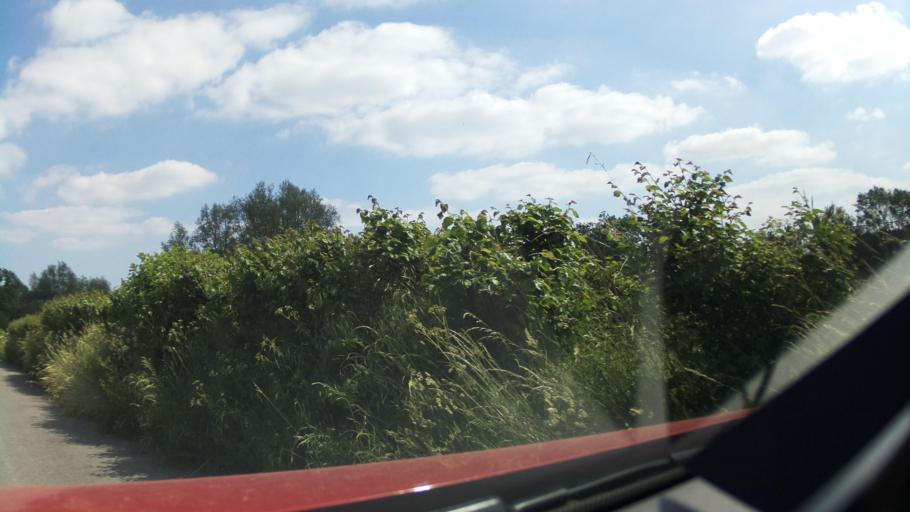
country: GB
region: England
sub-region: Wiltshire
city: Rushall
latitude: 51.2562
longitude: -1.7940
